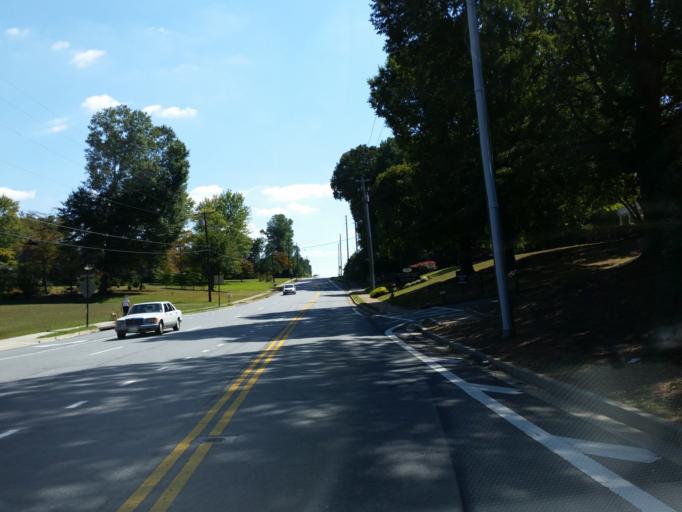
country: US
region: Georgia
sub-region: Cobb County
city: Marietta
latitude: 33.9784
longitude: -84.4616
